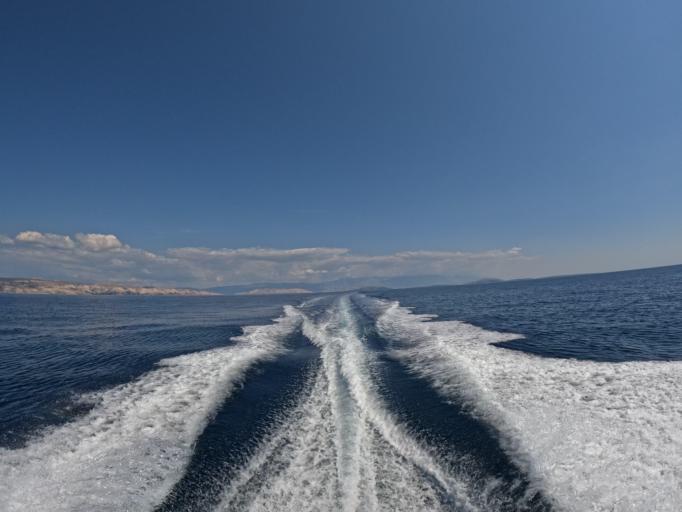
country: HR
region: Primorsko-Goranska
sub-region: Grad Krk
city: Krk
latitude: 44.9211
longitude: 14.5613
